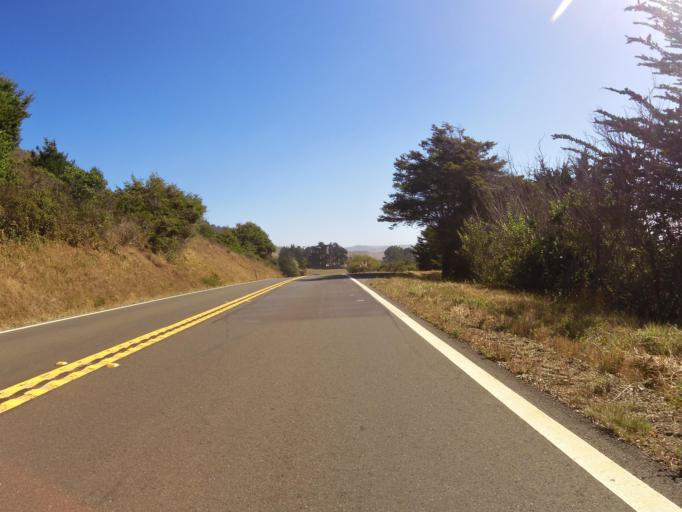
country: US
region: California
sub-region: Mendocino County
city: Fort Bragg
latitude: 39.5941
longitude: -123.7814
